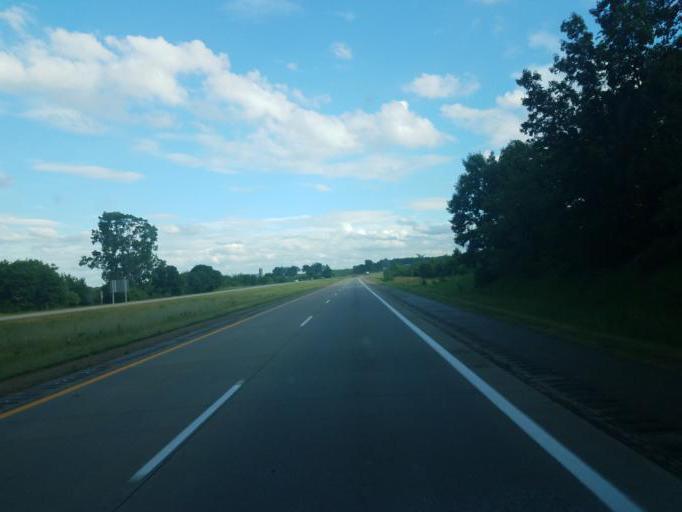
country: US
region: Indiana
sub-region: Steuben County
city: Fremont
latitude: 41.7745
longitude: -84.9889
